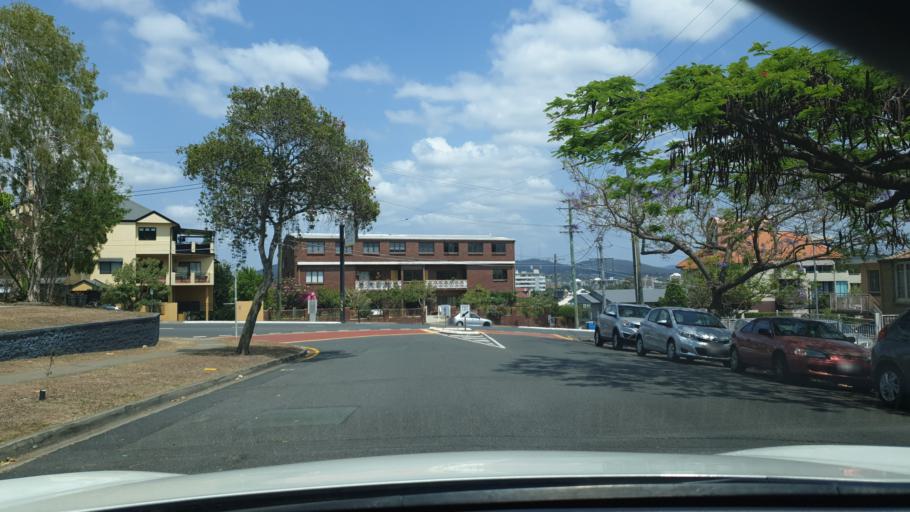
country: AU
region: Queensland
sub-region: Brisbane
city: South Brisbane
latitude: -27.4841
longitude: 153.0169
